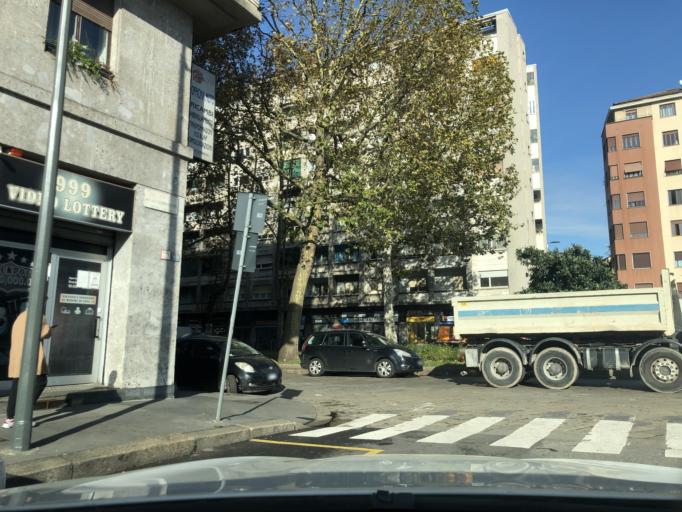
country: IT
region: Lombardy
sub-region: Citta metropolitana di Milano
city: Milano
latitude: 45.4905
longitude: 9.2068
